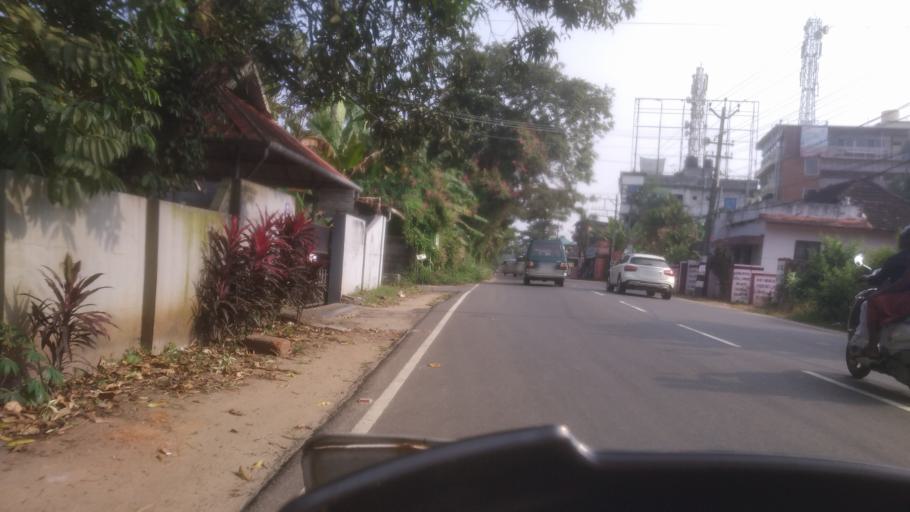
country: IN
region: Kerala
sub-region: Alappuzha
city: Arukutti
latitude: 9.9117
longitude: 76.3646
